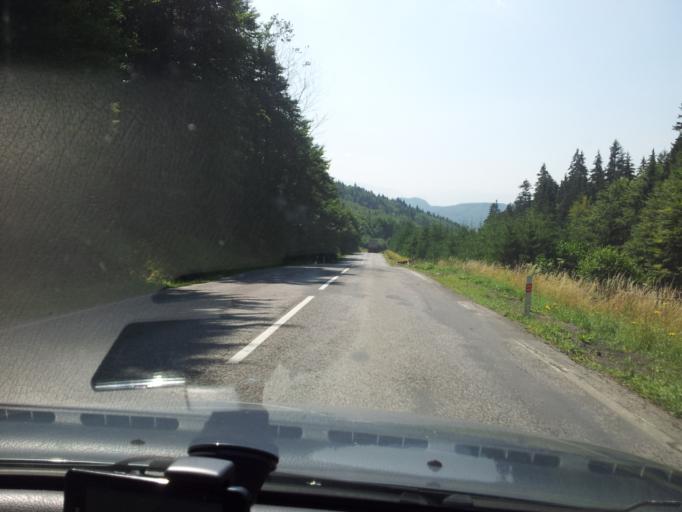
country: SK
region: Zilinsky
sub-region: Okres Dolny Kubin
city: Dolny Kubin
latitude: 49.3016
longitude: 19.3534
